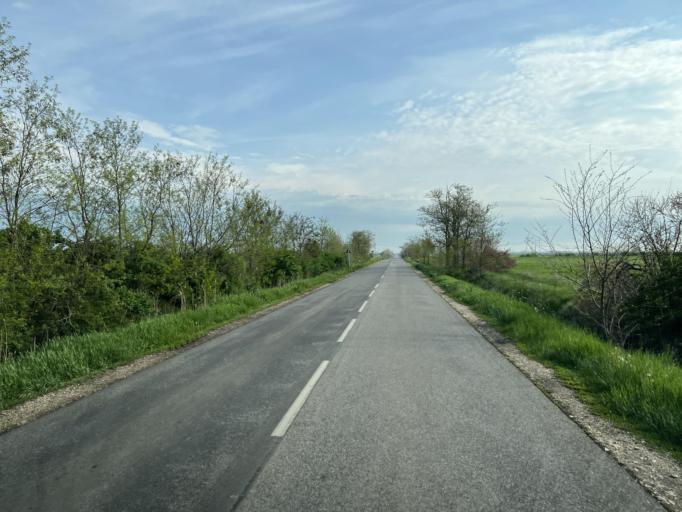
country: HU
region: Pest
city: Cegled
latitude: 47.2269
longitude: 19.7711
